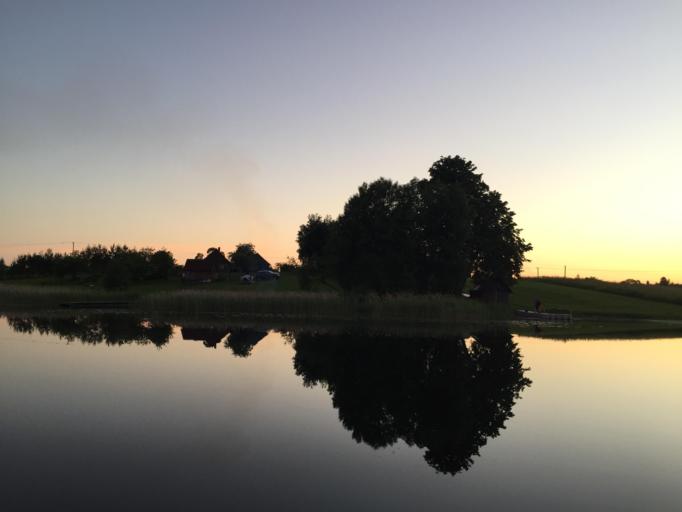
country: LV
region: Rezekne
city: Rezekne
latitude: 56.3680
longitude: 27.4117
